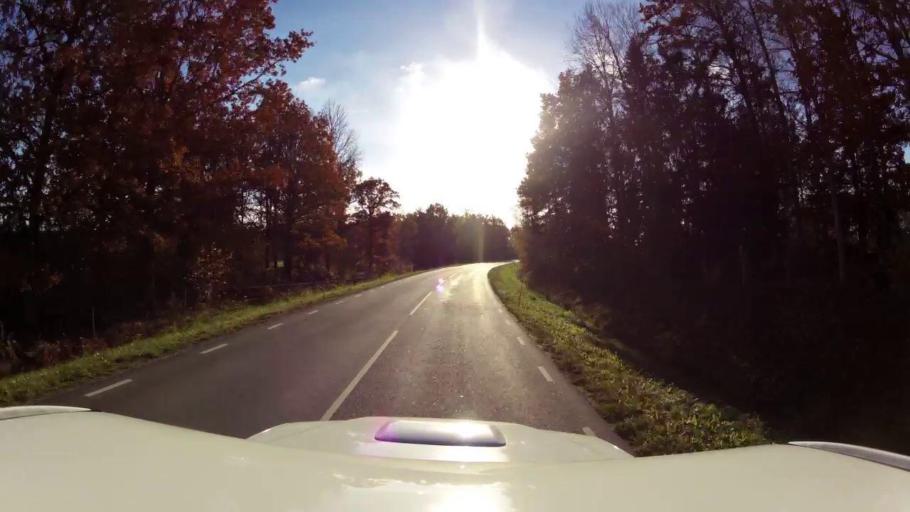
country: SE
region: OEstergoetland
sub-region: Linkopings Kommun
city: Vikingstad
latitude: 58.3080
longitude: 15.4898
